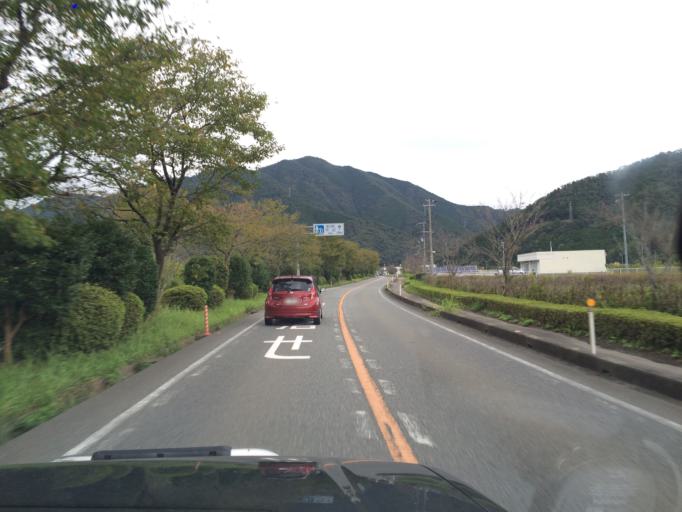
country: JP
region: Hyogo
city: Toyooka
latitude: 35.3774
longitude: 134.8135
